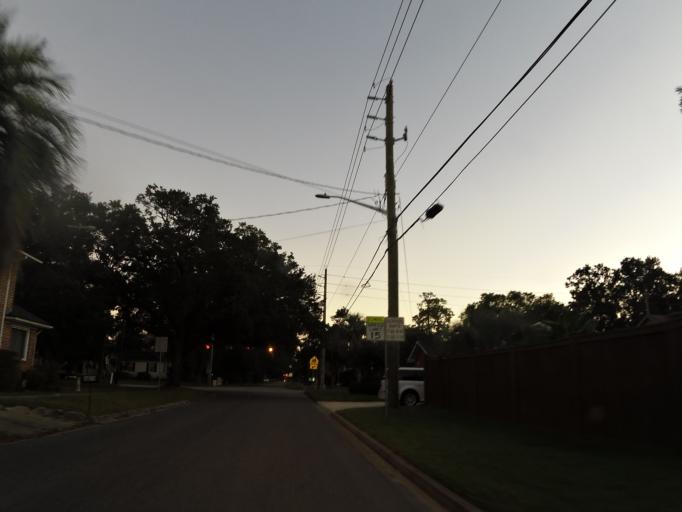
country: US
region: Florida
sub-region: Duval County
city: Jacksonville
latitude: 30.3073
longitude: -81.7223
